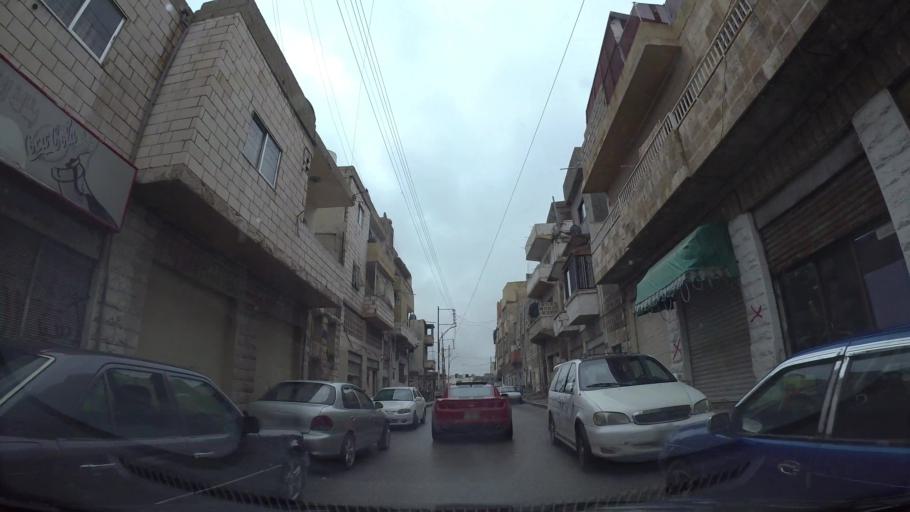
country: JO
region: Amman
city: Amman
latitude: 31.9473
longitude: 35.9232
